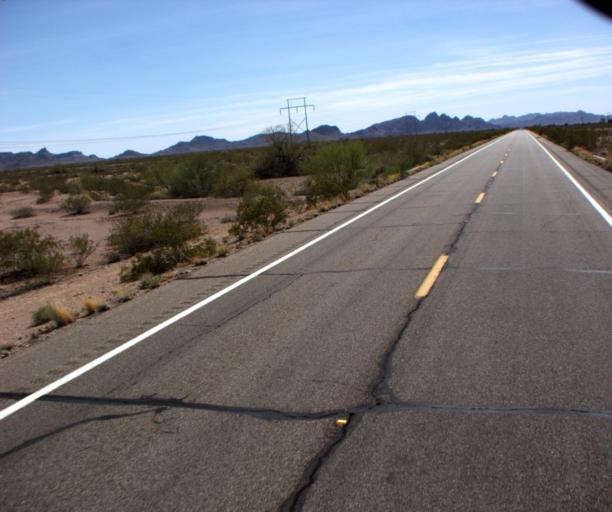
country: US
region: Arizona
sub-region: La Paz County
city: Quartzsite
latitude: 33.3645
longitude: -114.2171
